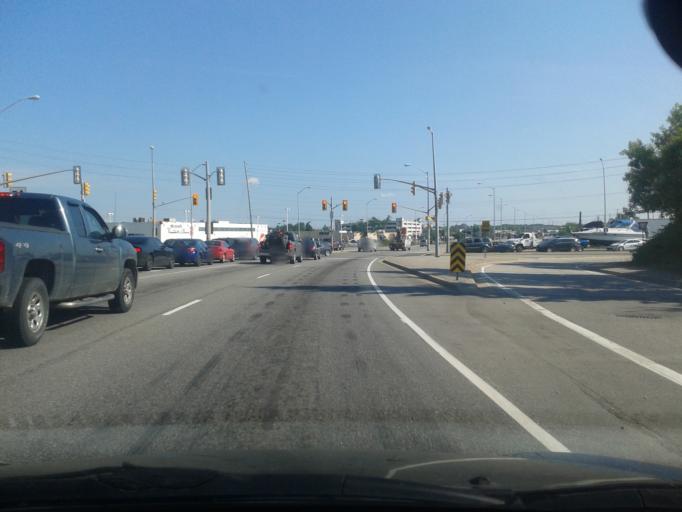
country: CA
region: Ontario
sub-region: Nipissing District
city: North Bay
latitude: 46.3189
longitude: -79.4438
